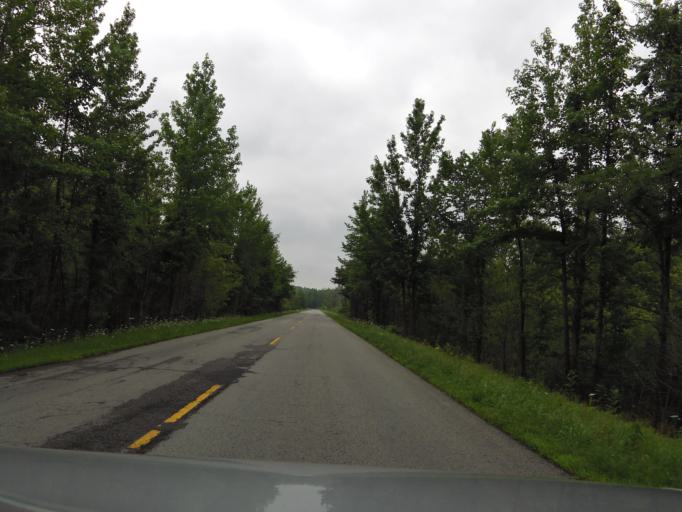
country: US
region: Kentucky
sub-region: Muhlenberg County
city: Morehead
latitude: 37.2872
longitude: -87.3044
